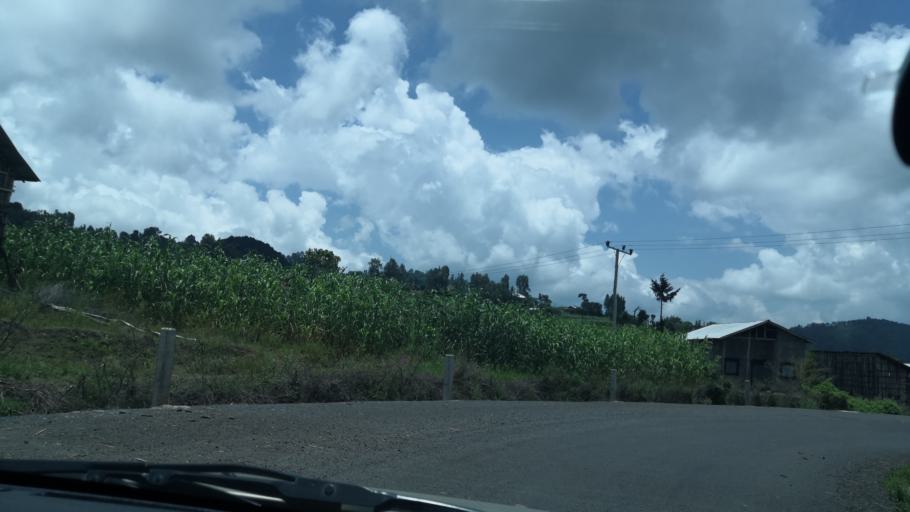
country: ET
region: Amhara
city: Abomsa
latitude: 10.3210
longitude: 39.8725
